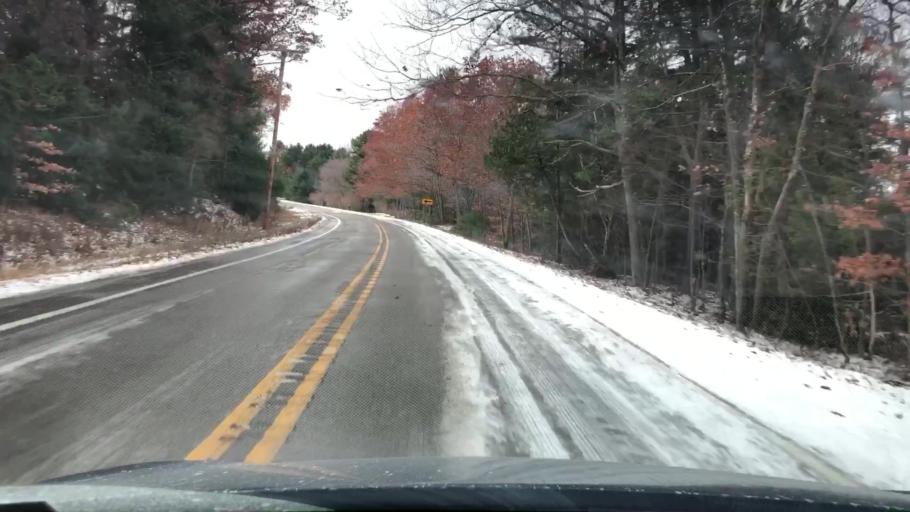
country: US
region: Michigan
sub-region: Antrim County
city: Elk Rapids
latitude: 44.9803
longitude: -85.5009
